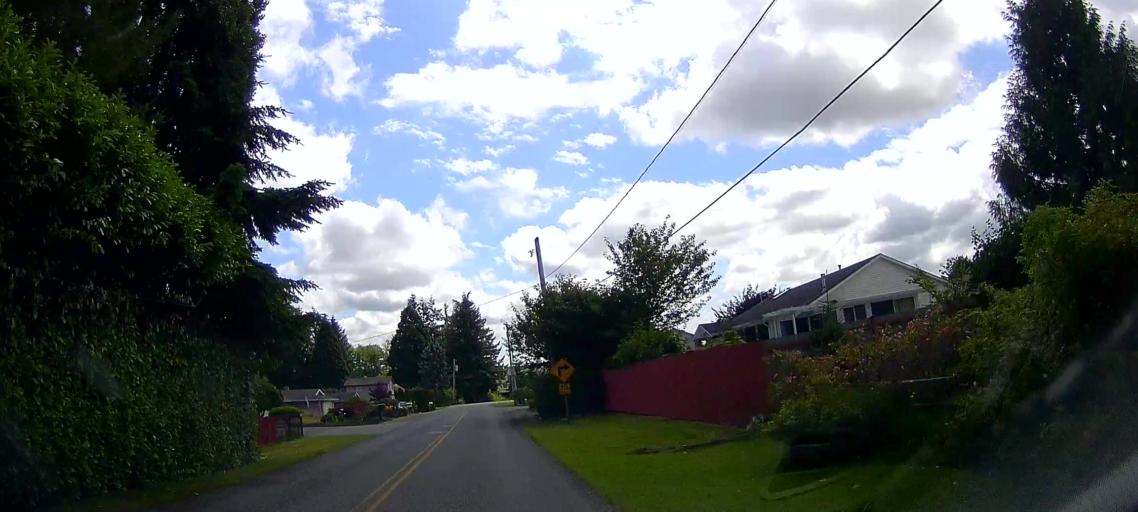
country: US
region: Washington
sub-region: Skagit County
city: Burlington
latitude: 48.4802
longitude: -122.3030
